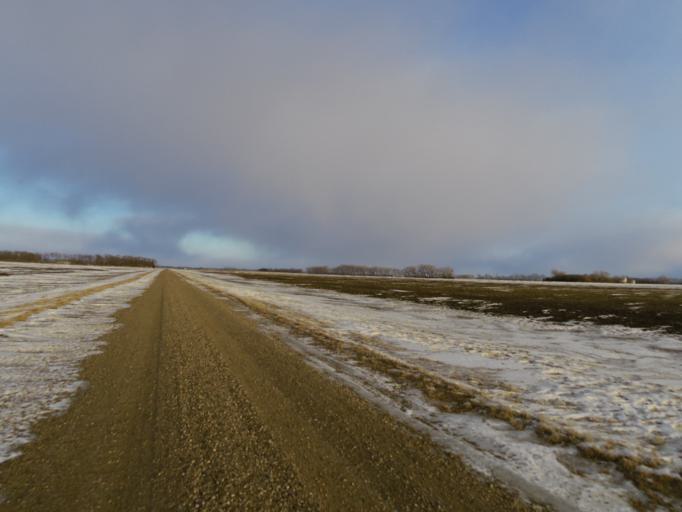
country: US
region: North Dakota
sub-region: Walsh County
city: Grafton
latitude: 48.3976
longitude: -97.2199
